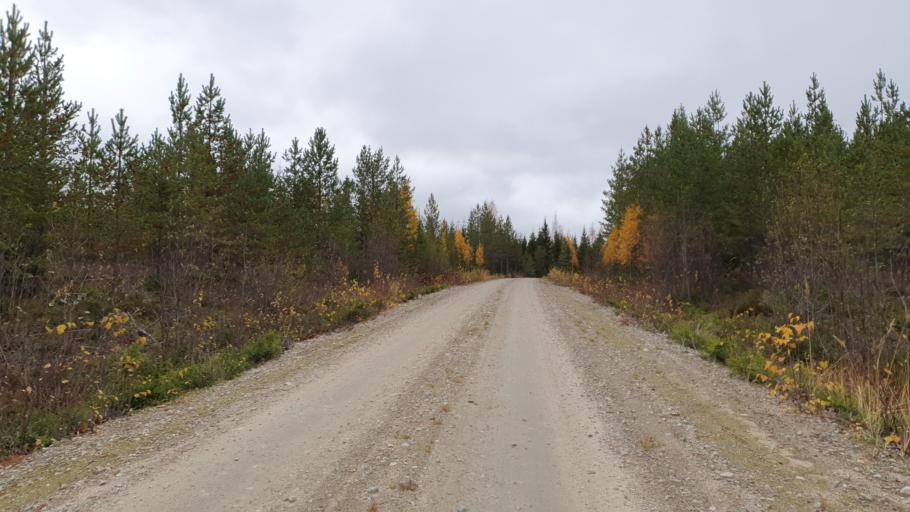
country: FI
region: Kainuu
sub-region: Kehys-Kainuu
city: Kuhmo
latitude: 64.4583
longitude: 29.6058
